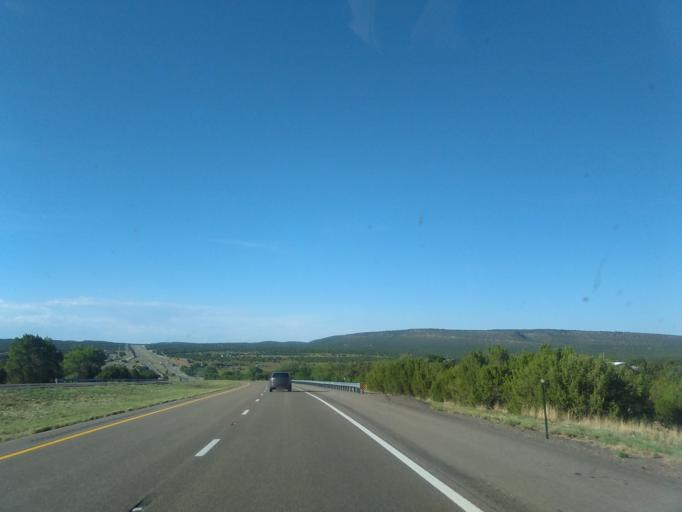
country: US
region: New Mexico
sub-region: San Miguel County
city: Las Vegas
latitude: 35.4492
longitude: -105.2798
